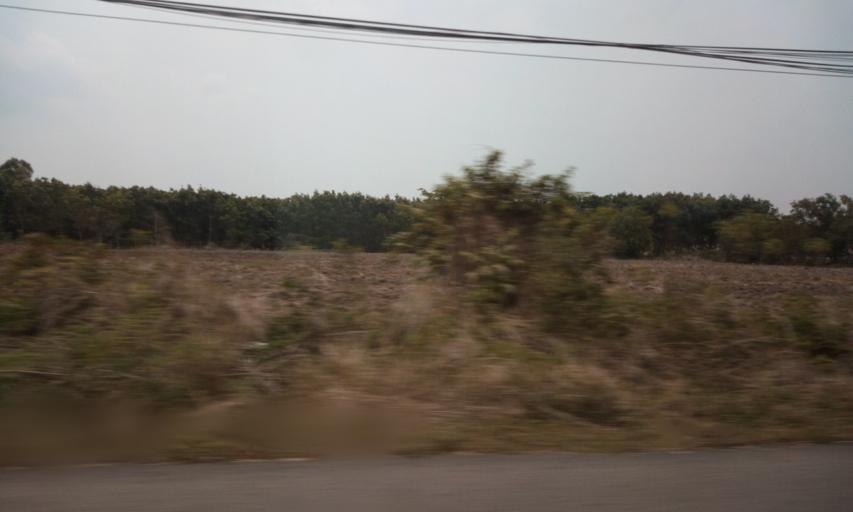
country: TH
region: Phayao
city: Phu Sang
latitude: 19.5835
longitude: 100.3096
